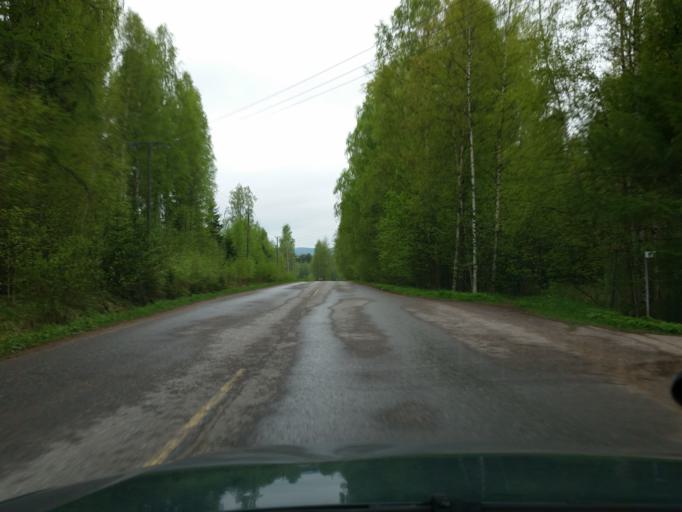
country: FI
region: Uusimaa
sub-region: Helsinki
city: Karjalohja
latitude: 60.1439
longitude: 23.8470
